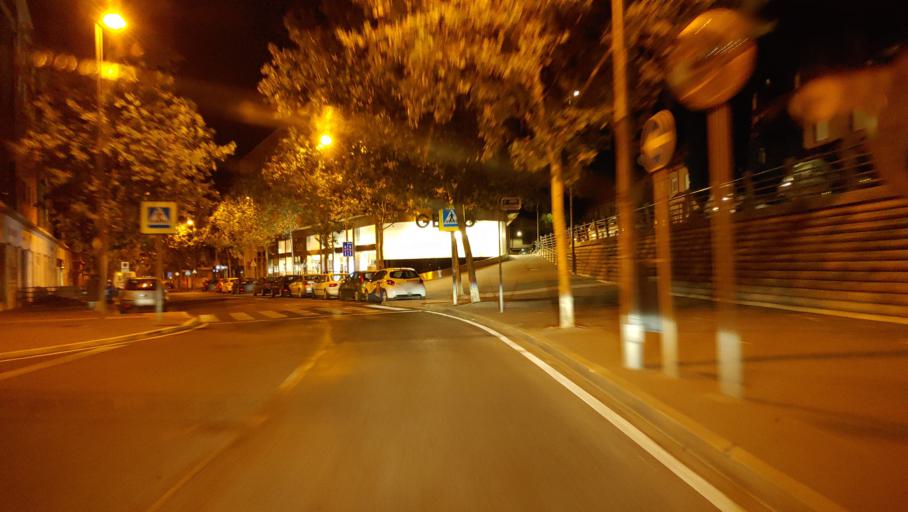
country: ES
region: Castille-La Mancha
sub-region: Provincia de Ciudad Real
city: Ciudad Real
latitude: 38.9789
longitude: -3.9278
